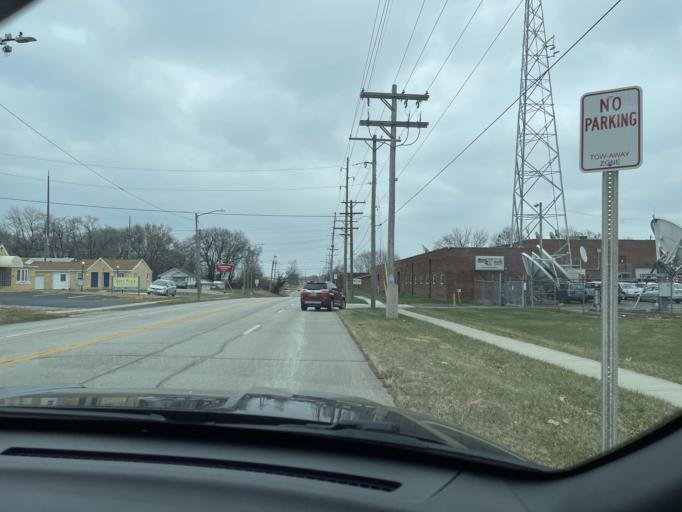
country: US
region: Illinois
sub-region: Sangamon County
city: Grandview
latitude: 39.7946
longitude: -89.6177
